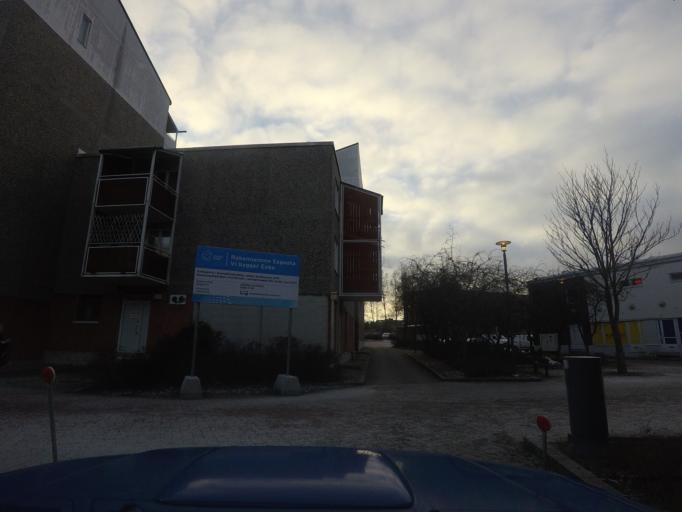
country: FI
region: Uusimaa
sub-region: Helsinki
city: Espoo
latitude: 60.2082
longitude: 24.6628
